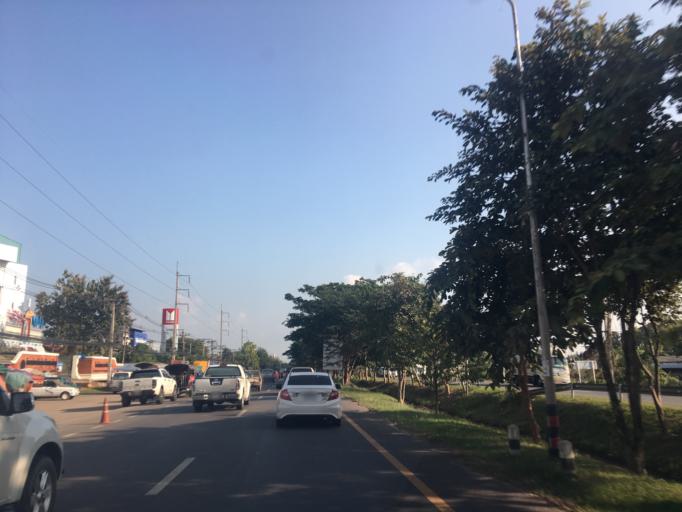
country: TH
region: Phayao
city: Phayao
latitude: 19.1694
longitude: 99.9081
